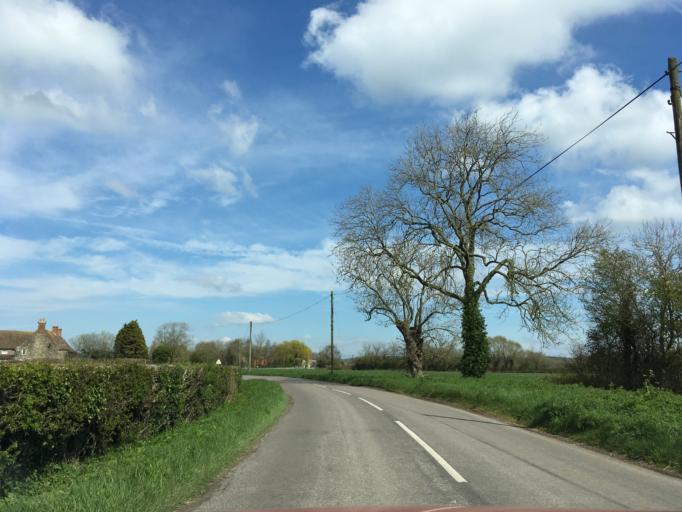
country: GB
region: England
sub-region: South Gloucestershire
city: Almondsbury
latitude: 51.5666
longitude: -2.6147
